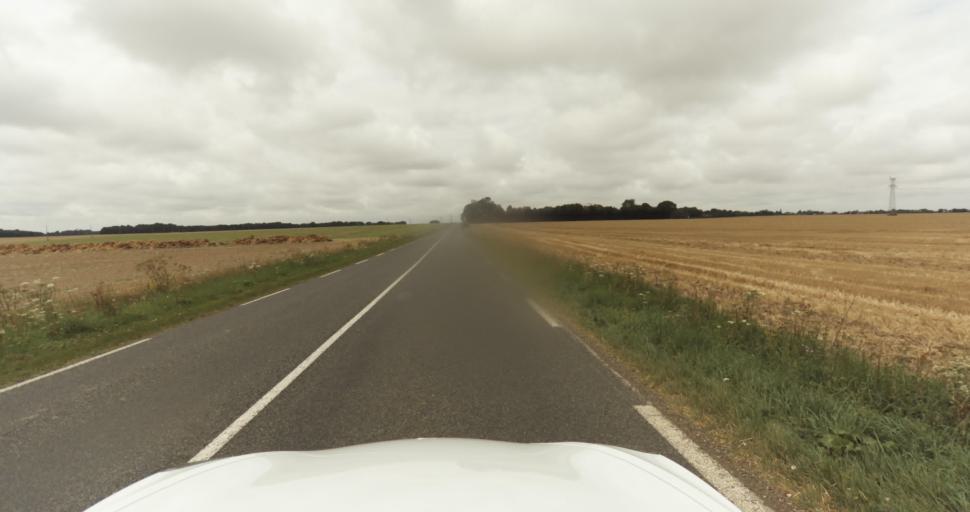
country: FR
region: Haute-Normandie
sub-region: Departement de l'Eure
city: Claville
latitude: 49.0353
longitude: 1.0542
